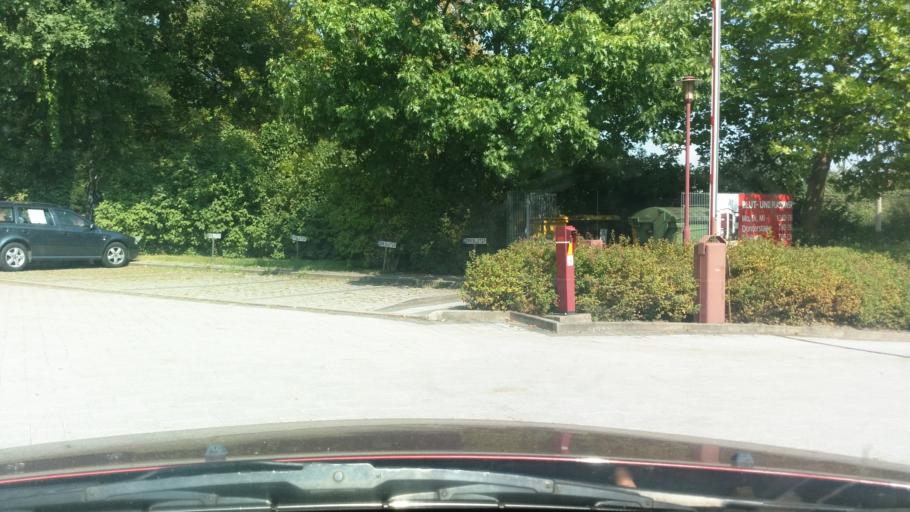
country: DE
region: Saxony
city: Goerlitz
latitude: 51.1596
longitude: 14.9733
